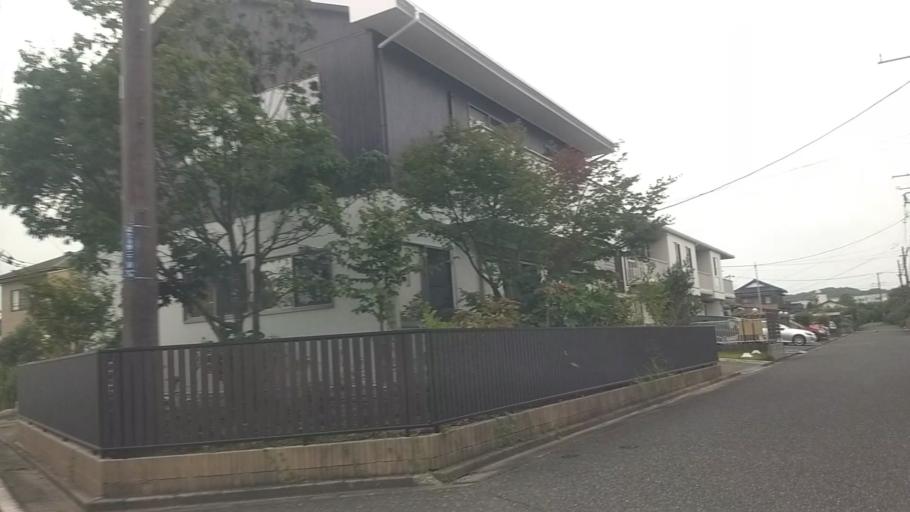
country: JP
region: Chiba
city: Kisarazu
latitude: 35.3862
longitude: 139.9660
